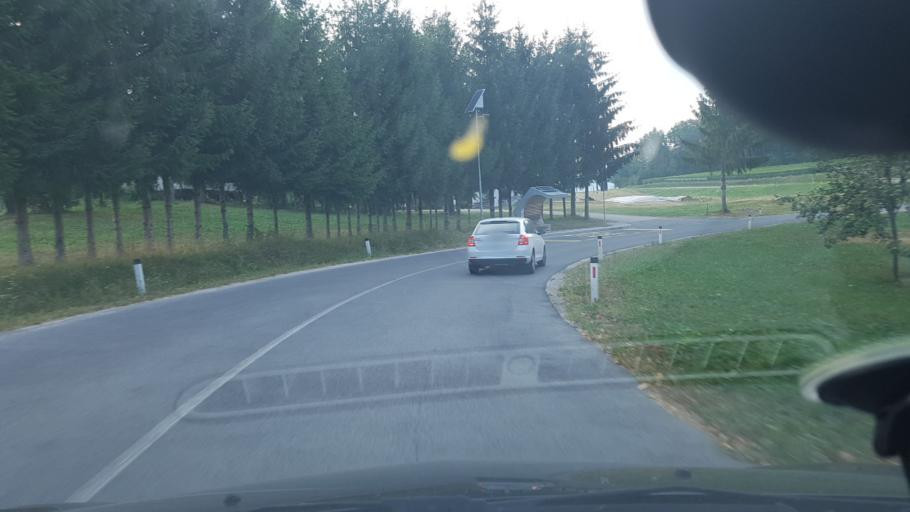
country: SI
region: Kozje
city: Kozje
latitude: 46.0921
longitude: 15.5693
